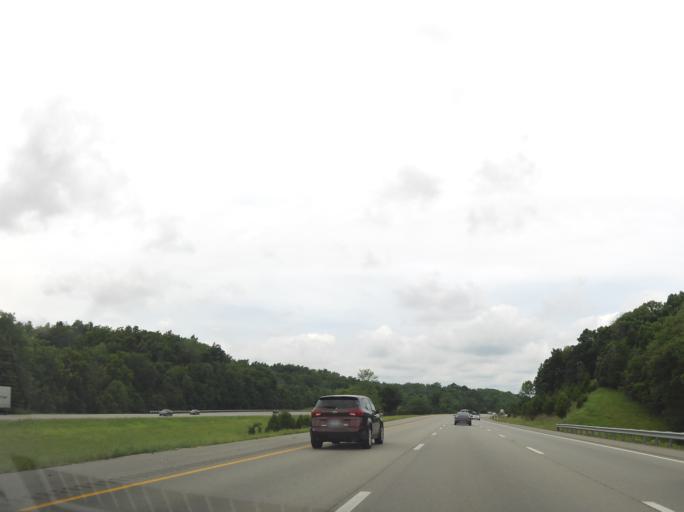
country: US
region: Kentucky
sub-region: Scott County
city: Georgetown
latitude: 38.3243
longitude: -84.5601
